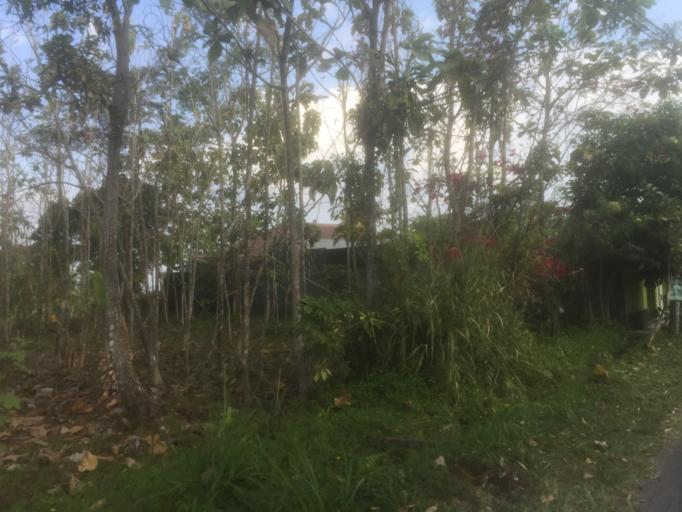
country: ID
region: Daerah Istimewa Yogyakarta
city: Sleman
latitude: -7.6401
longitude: 110.4254
